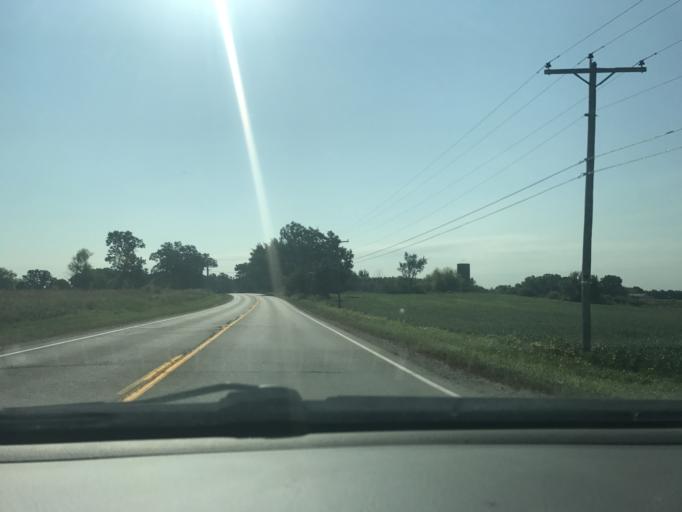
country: US
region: Illinois
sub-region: Kane County
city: Pingree Grove
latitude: 42.0710
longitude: -88.4386
